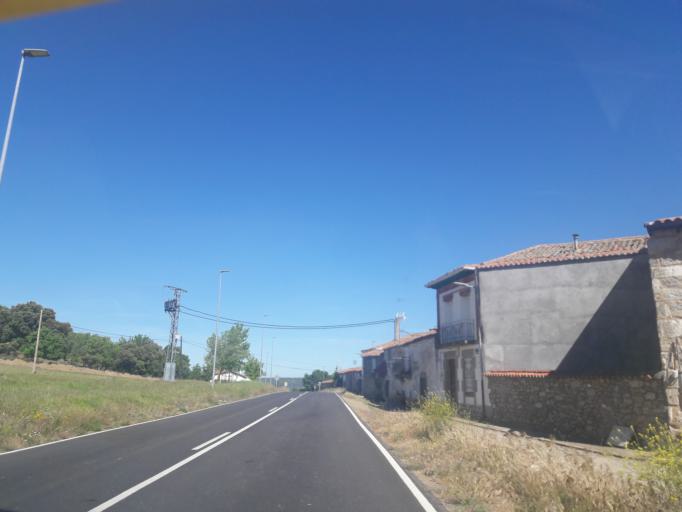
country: ES
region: Castille and Leon
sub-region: Provincia de Salamanca
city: Nava de Bejar
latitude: 40.4948
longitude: -5.6639
